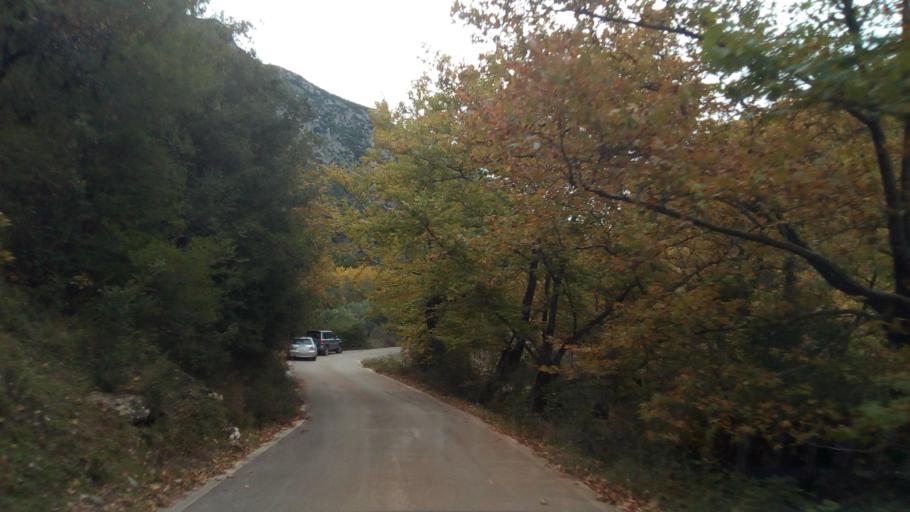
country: GR
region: West Greece
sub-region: Nomos Aitolias kai Akarnanias
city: Thermo
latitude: 38.5974
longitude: 21.8521
